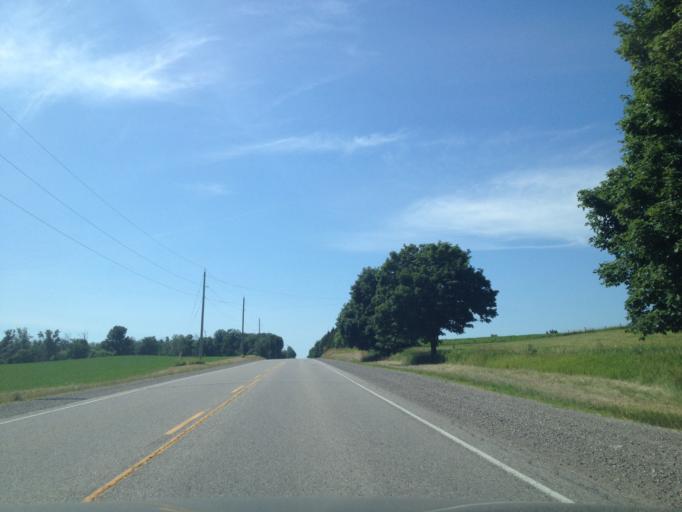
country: CA
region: Ontario
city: Stratford
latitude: 43.4716
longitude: -80.8044
